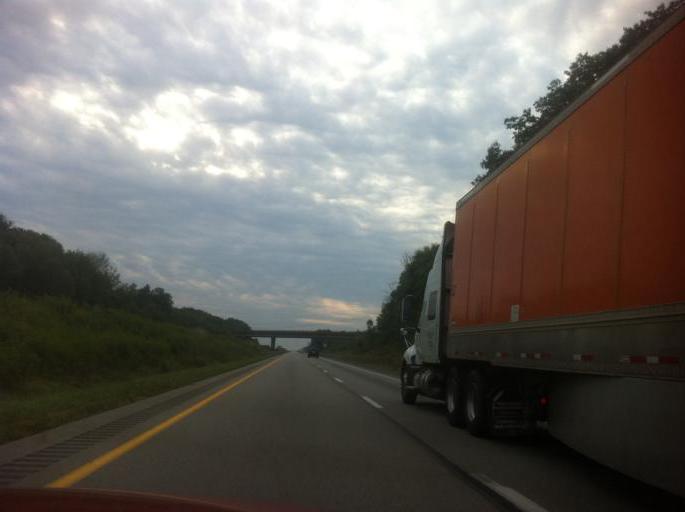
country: US
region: Pennsylvania
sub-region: Mercer County
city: Grove City
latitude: 41.1982
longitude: -79.8979
